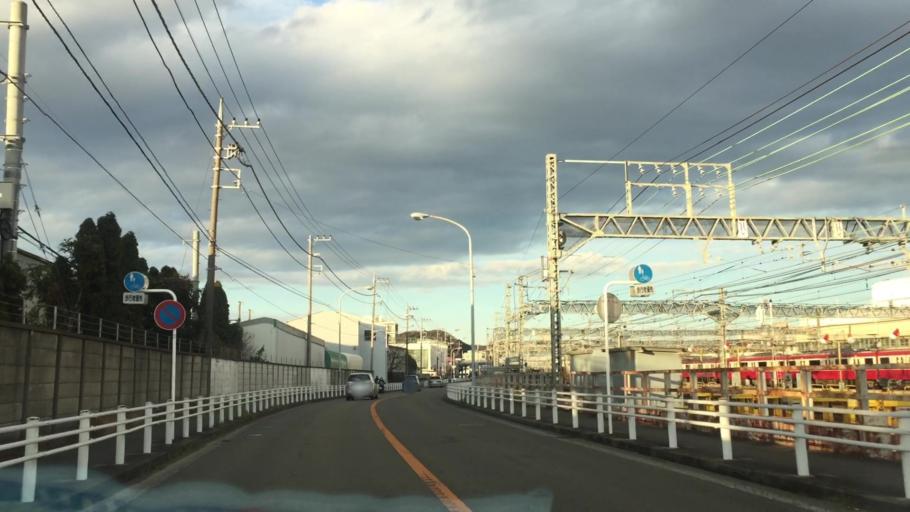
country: JP
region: Kanagawa
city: Zushi
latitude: 35.3365
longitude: 139.6199
